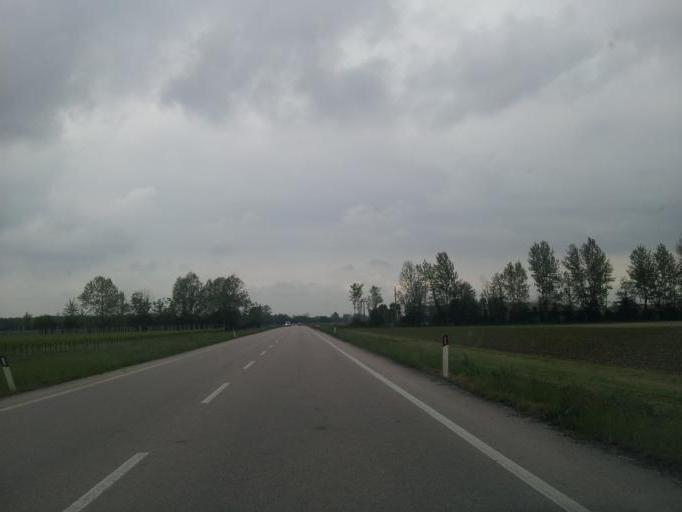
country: IT
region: Friuli Venezia Giulia
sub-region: Provincia di Udine
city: Codroipo
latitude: 45.9292
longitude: 12.9834
